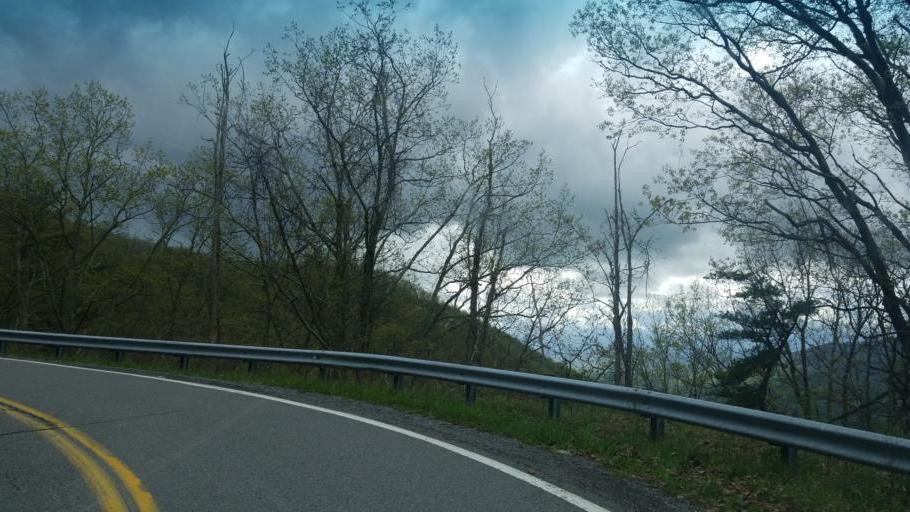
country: US
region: Virginia
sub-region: Tazewell County
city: Tazewell
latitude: 37.0000
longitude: -81.5324
